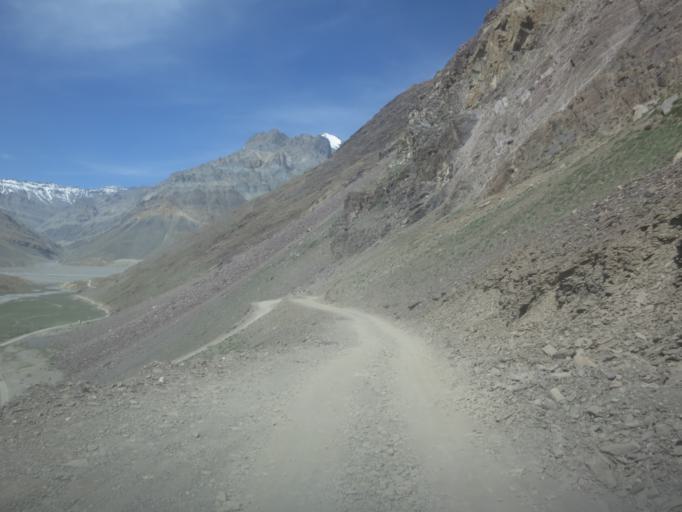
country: IN
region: Himachal Pradesh
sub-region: Kulu
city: Manali
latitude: 32.4385
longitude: 77.6838
